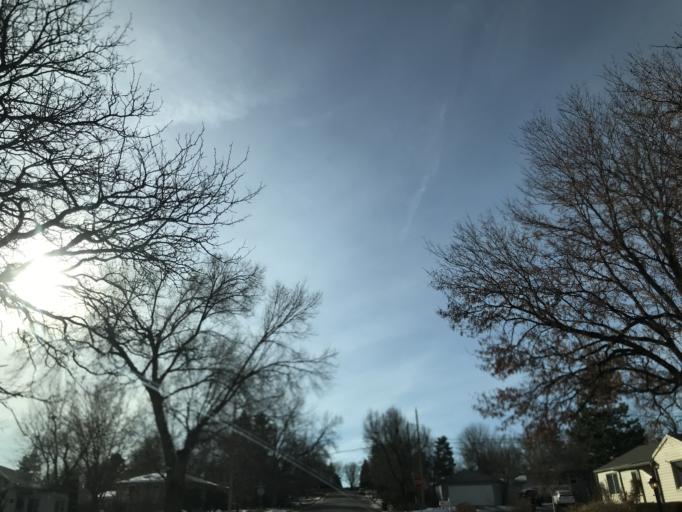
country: US
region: Colorado
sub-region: Arapahoe County
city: Littleton
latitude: 39.5993
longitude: -105.0094
